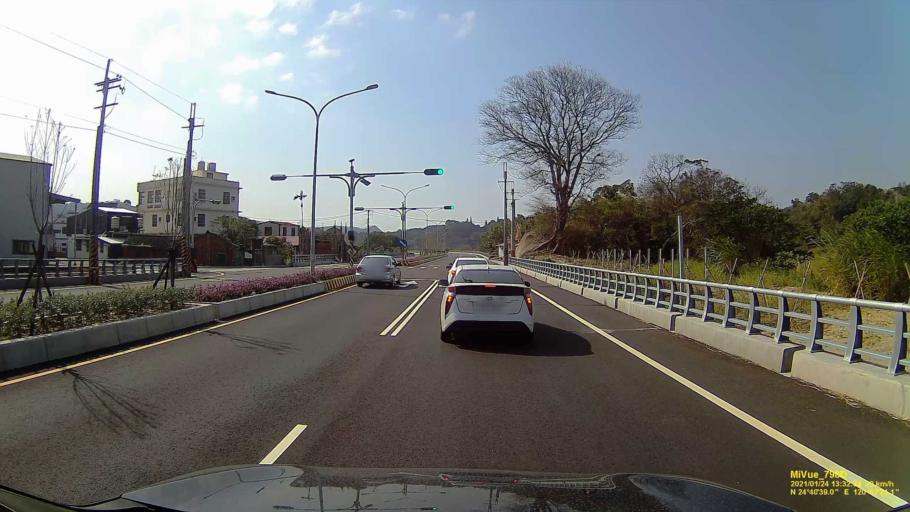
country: TW
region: Taiwan
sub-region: Hsinchu
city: Hsinchu
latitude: 24.6775
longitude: 120.9556
